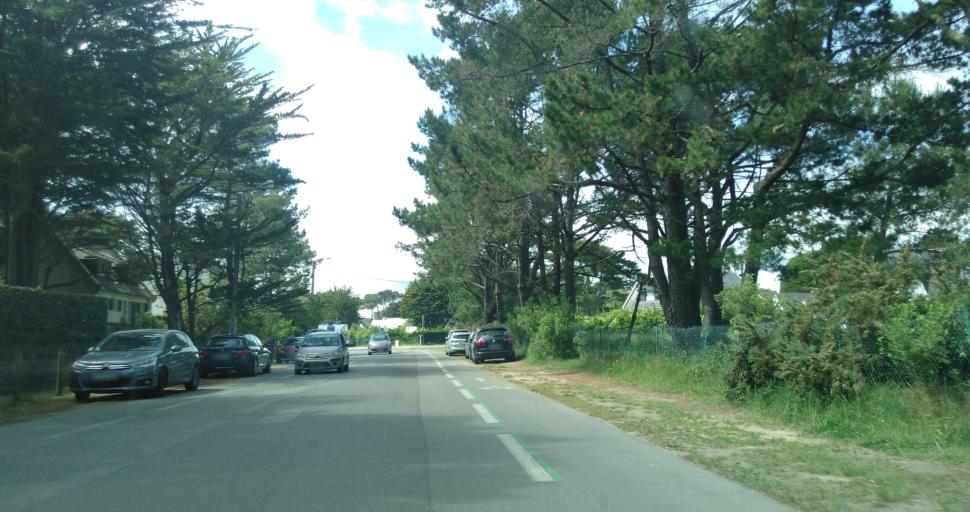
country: FR
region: Brittany
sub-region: Departement du Morbihan
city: Carnac
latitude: 47.5747
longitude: -3.0544
